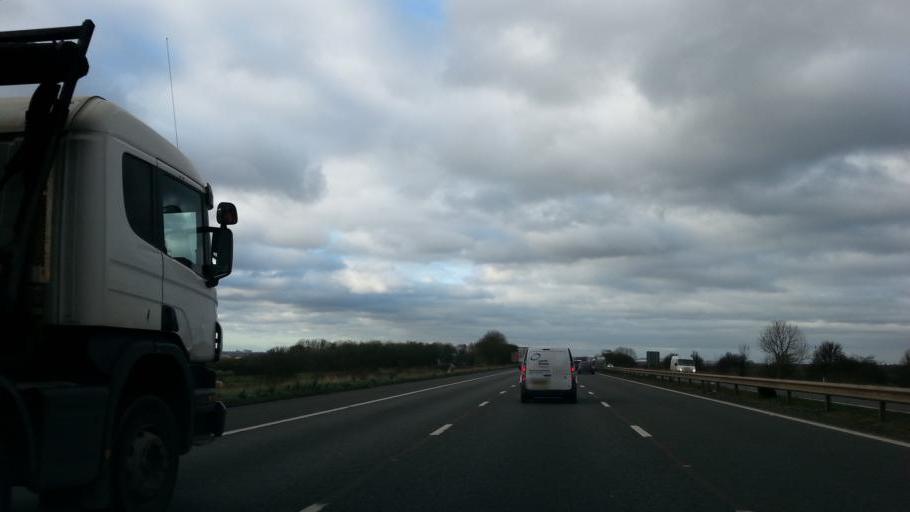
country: GB
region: England
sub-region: Warwickshire
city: Brandon
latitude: 52.4358
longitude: -1.3732
